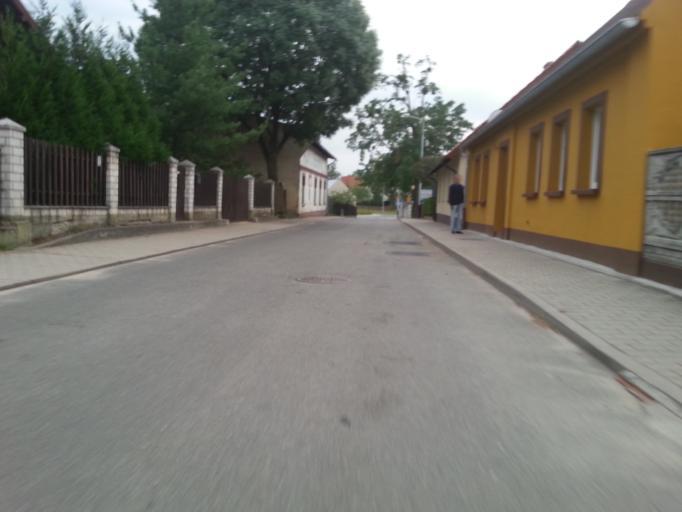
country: PL
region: Lower Silesian Voivodeship
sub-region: Powiat olesnicki
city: Twardogora
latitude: 51.3683
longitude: 17.4622
